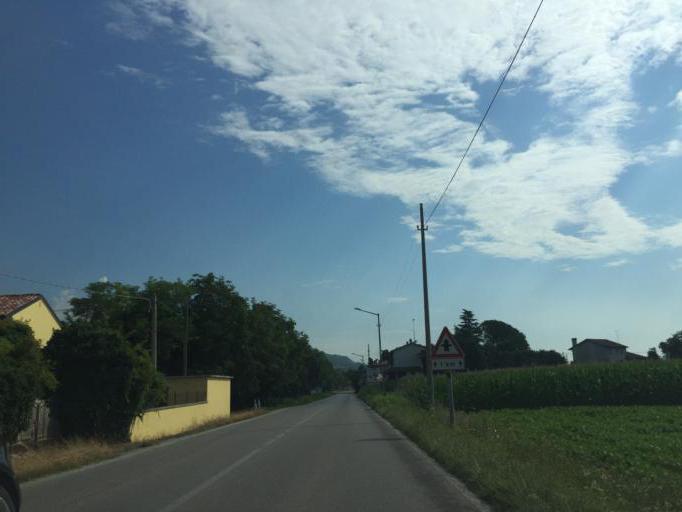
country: IT
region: Veneto
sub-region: Provincia di Treviso
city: Cordignano
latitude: 45.9592
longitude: 12.4314
